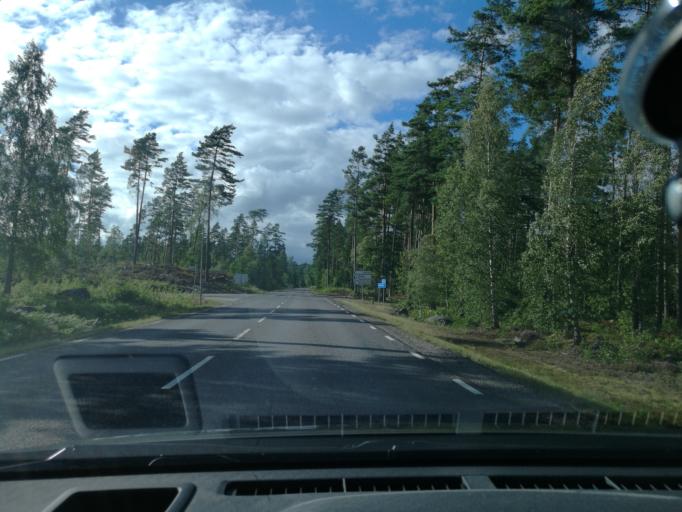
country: SE
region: Kronoberg
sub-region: Vaxjo Kommun
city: Braas
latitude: 57.0596
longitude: 15.0362
